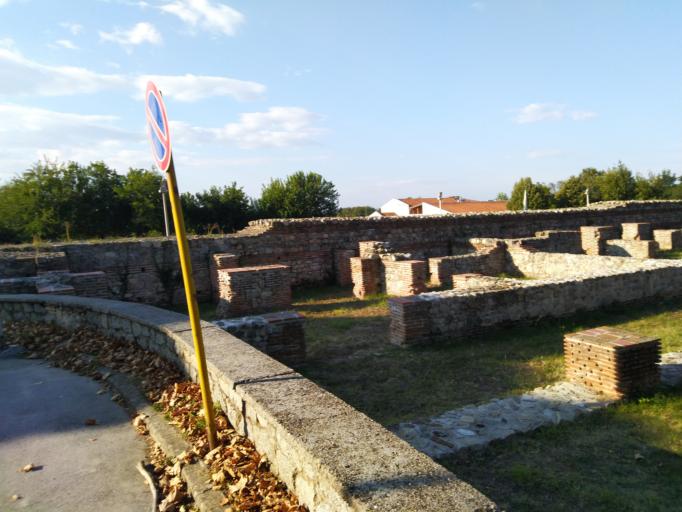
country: BG
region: Plovdiv
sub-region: Obshtina Khisarya
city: Khisarya
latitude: 42.4989
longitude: 24.7055
